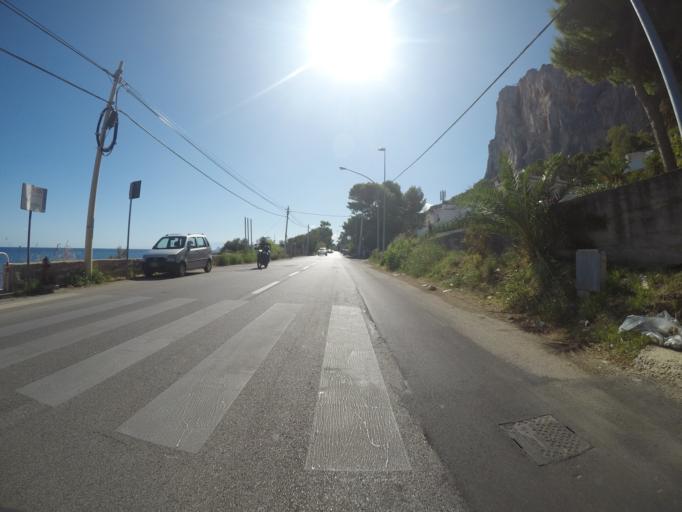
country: IT
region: Sicily
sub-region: Palermo
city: Palermo
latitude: 38.1862
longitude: 13.3612
